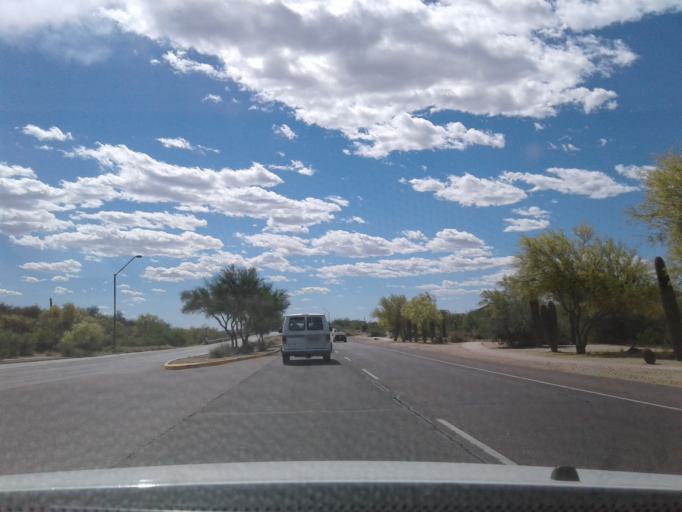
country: US
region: Arizona
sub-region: Maricopa County
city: Anthem
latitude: 33.7984
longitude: -112.1207
